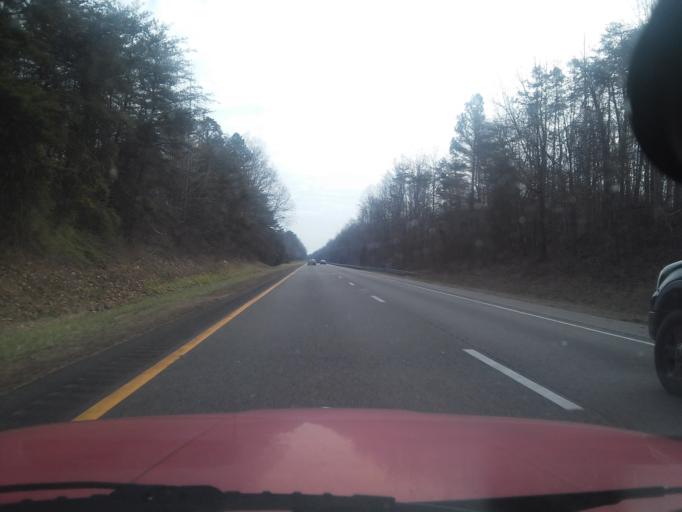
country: US
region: Virginia
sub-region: Goochland County
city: Goochland
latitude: 37.8122
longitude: -77.9375
